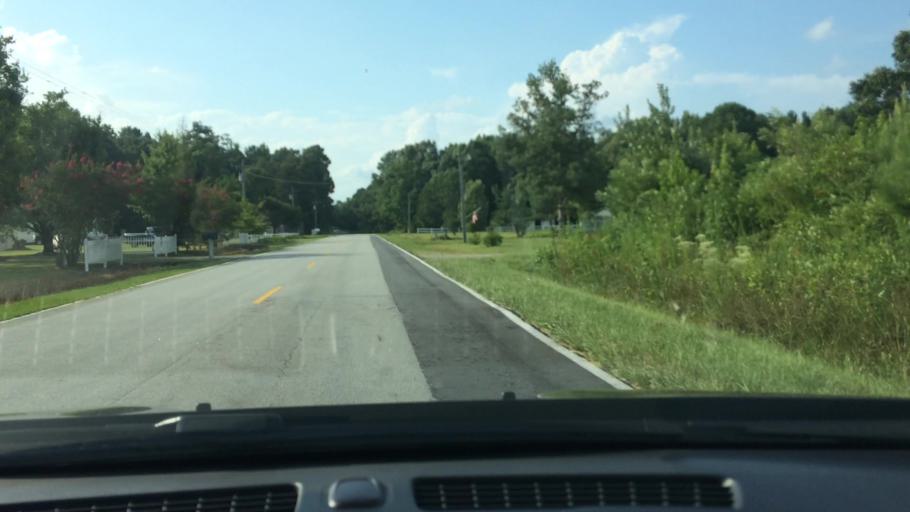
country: US
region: North Carolina
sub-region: Beaufort County
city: River Road
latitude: 35.4475
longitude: -77.0150
